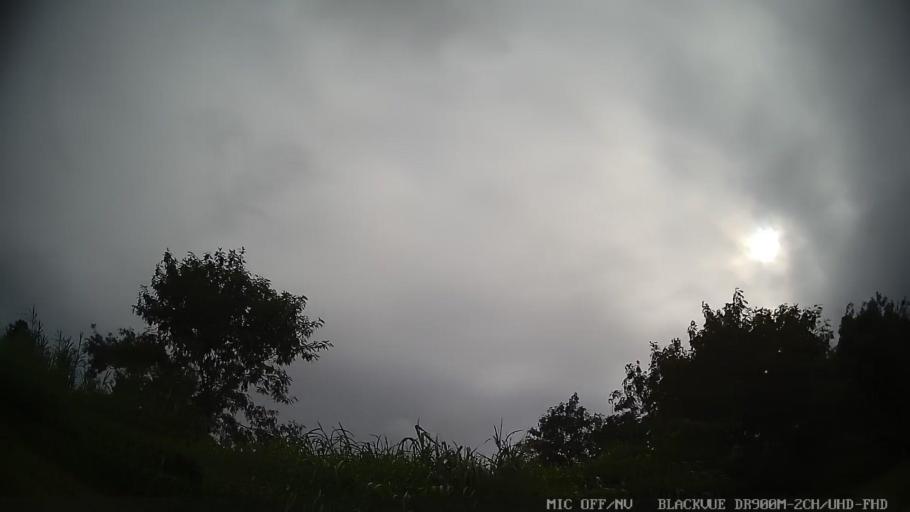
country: BR
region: Sao Paulo
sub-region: Osasco
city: Osasco
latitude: -23.4819
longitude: -46.7317
